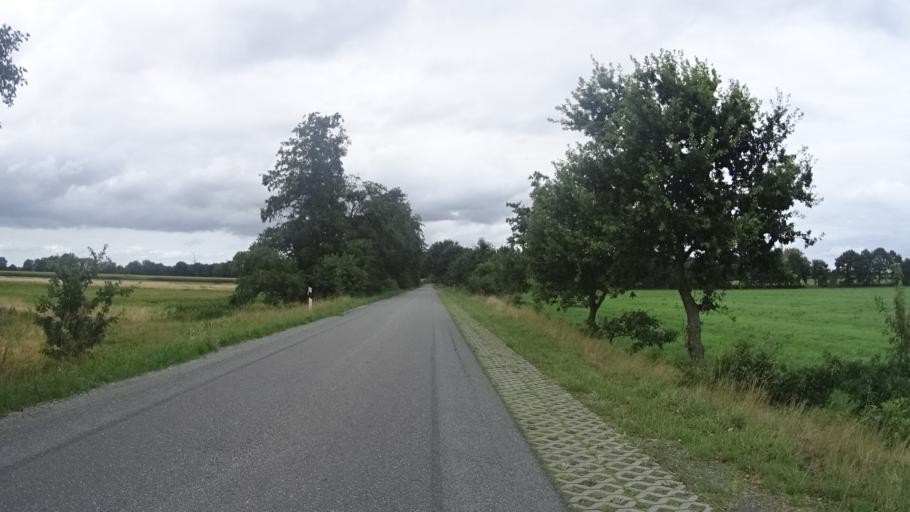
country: DE
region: Lower Saxony
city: Stinstedt
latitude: 53.6497
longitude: 8.9619
